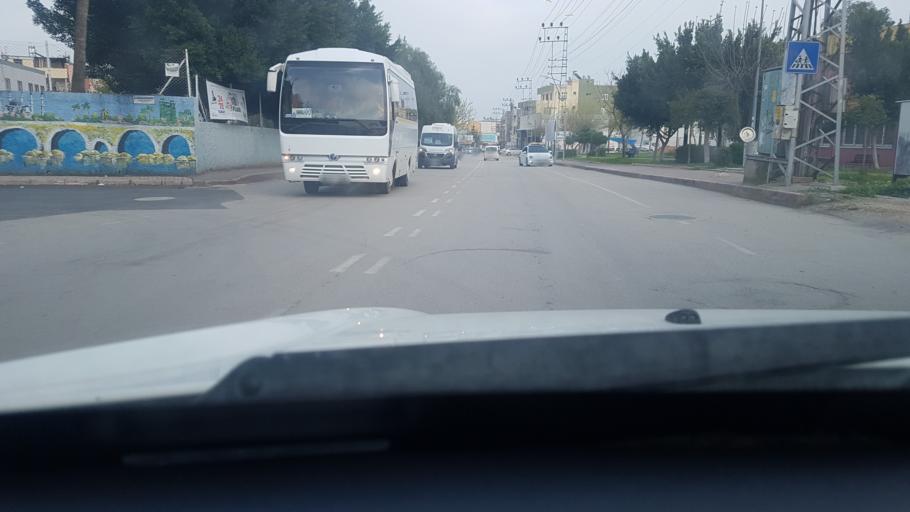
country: TR
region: Adana
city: Seyhan
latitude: 37.0161
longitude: 35.2735
